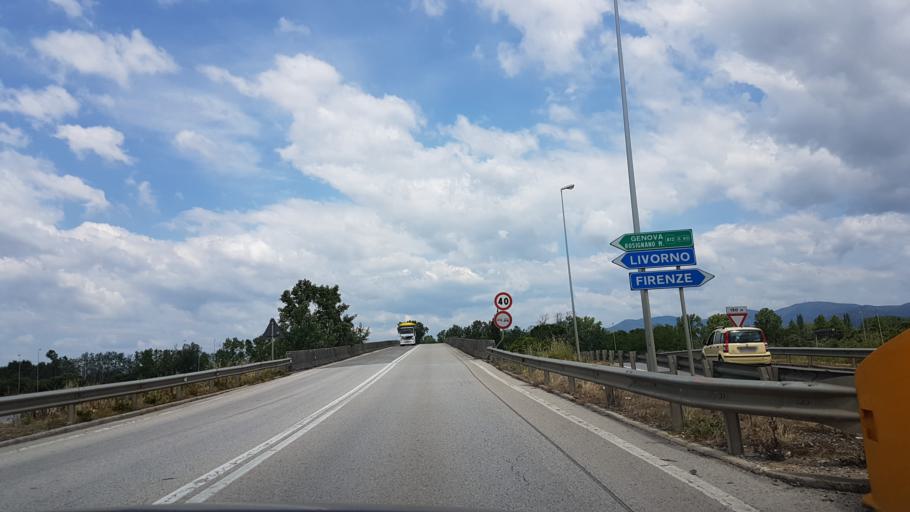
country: IT
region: Tuscany
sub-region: Provincia di Livorno
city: Vicarello
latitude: 43.6214
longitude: 10.4664
